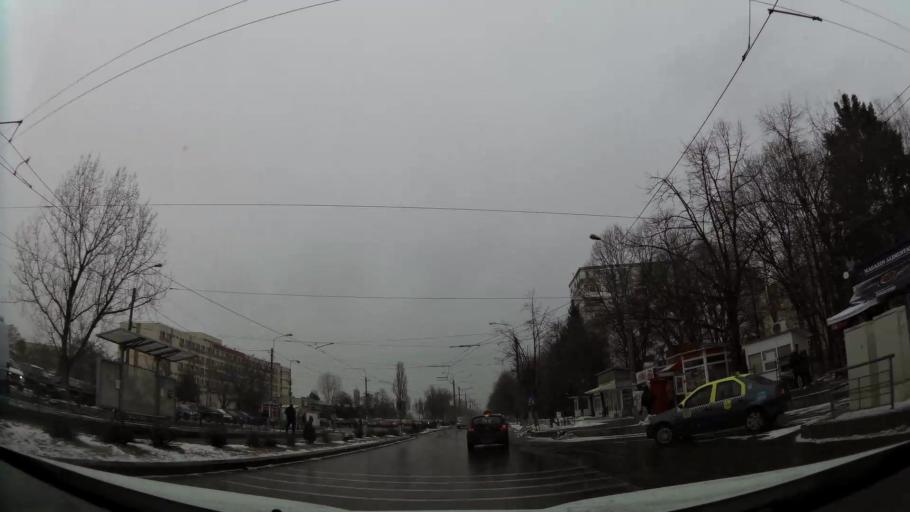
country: RO
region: Prahova
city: Ploiesti
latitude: 44.9630
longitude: 26.0073
